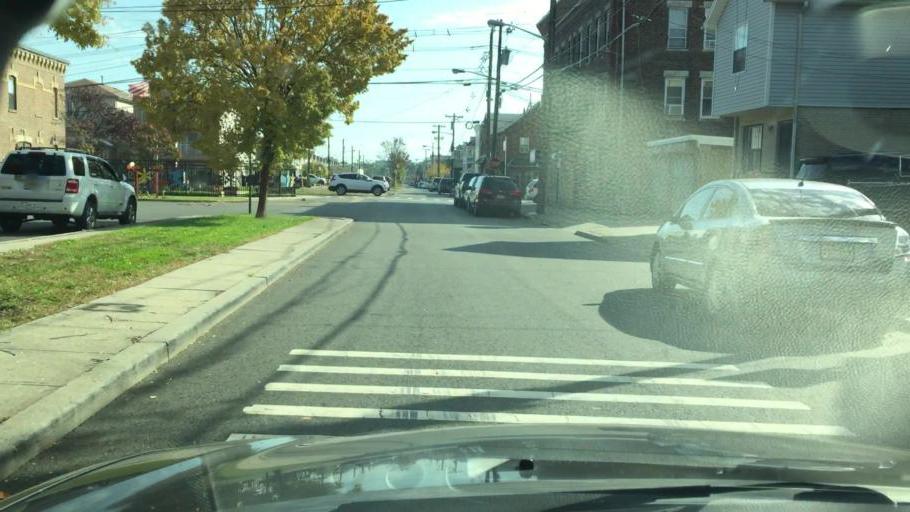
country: US
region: New Jersey
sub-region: Union County
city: Elizabeth
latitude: 40.6539
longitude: -74.1838
